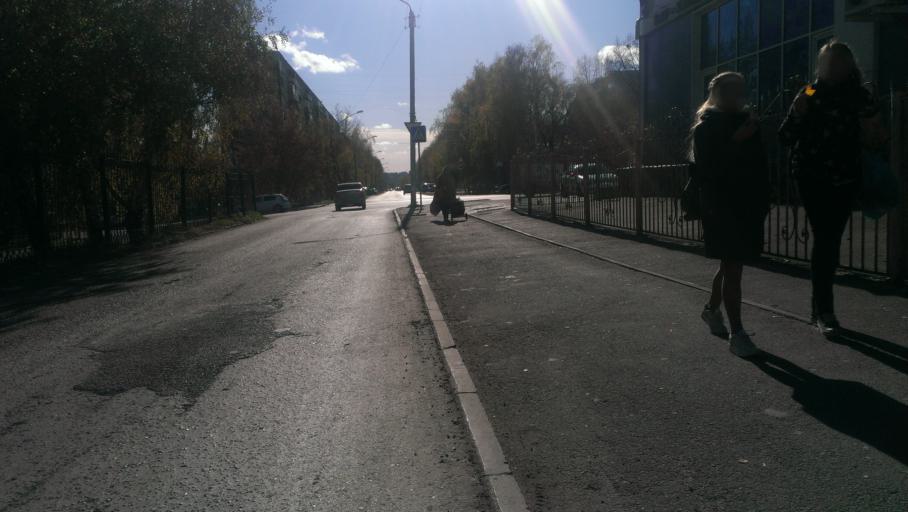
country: RU
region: Altai Krai
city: Novosilikatnyy
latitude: 53.3560
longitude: 83.6780
